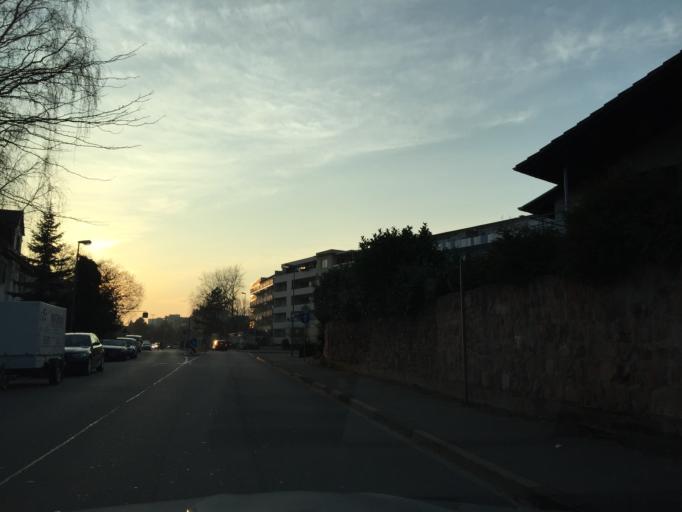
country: DE
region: Baden-Wuerttemberg
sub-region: Karlsruhe Region
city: Heidelberg
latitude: 49.4127
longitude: 8.6801
